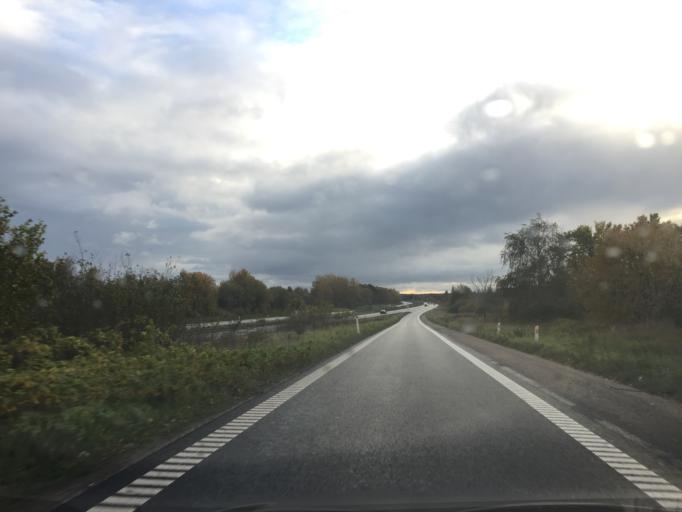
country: DK
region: Capital Region
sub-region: Fredensborg Kommune
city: Niva
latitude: 55.9664
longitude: 12.4891
